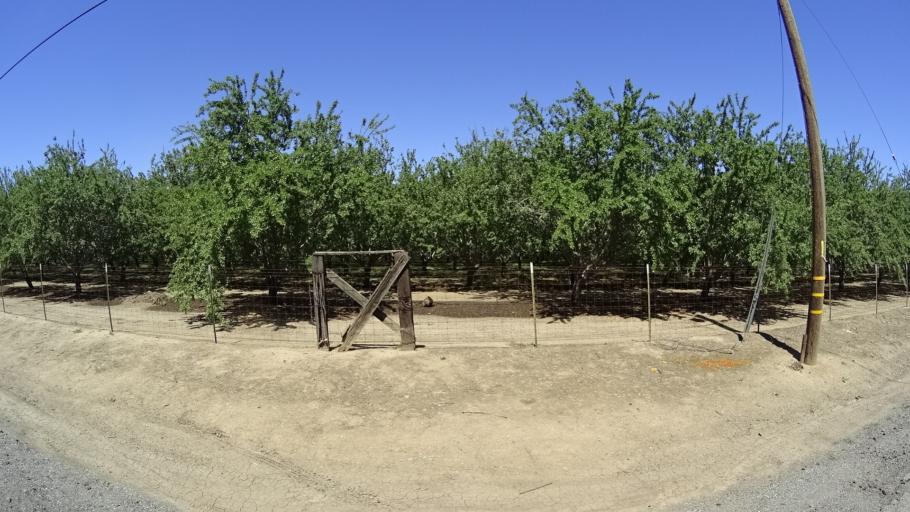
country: US
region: California
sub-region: Glenn County
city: Orland
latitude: 39.7322
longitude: -122.1116
